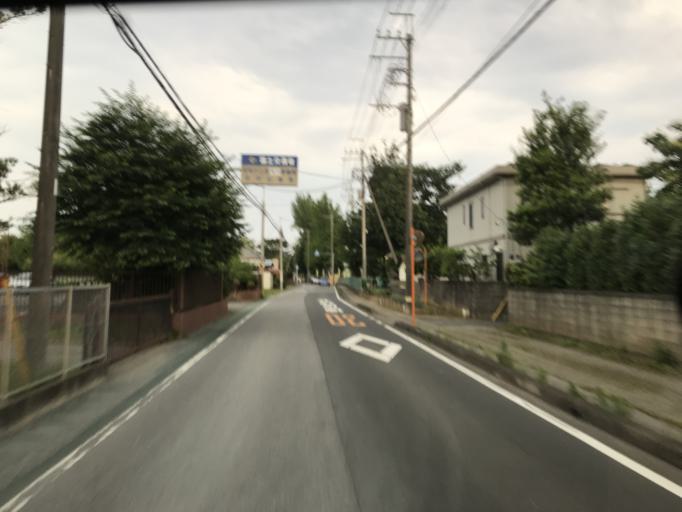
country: JP
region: Chiba
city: Noda
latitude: 35.9622
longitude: 139.8851
